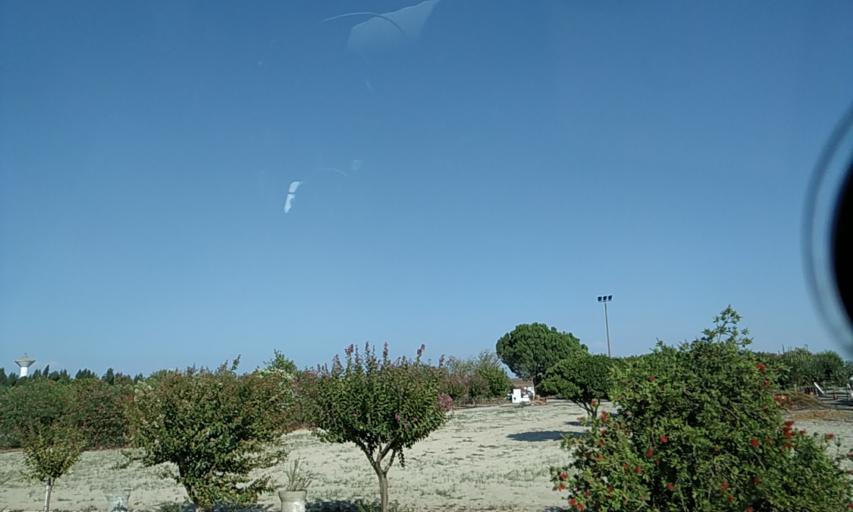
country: PT
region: Santarem
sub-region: Coruche
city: Coruche
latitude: 38.8252
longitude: -8.5653
